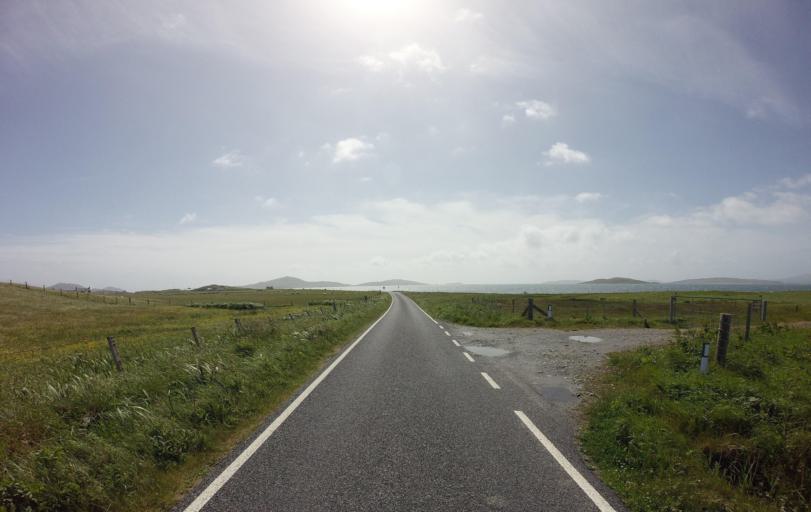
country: GB
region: Scotland
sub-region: Eilean Siar
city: Isle of South Uist
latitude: 57.1056
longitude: -7.3672
